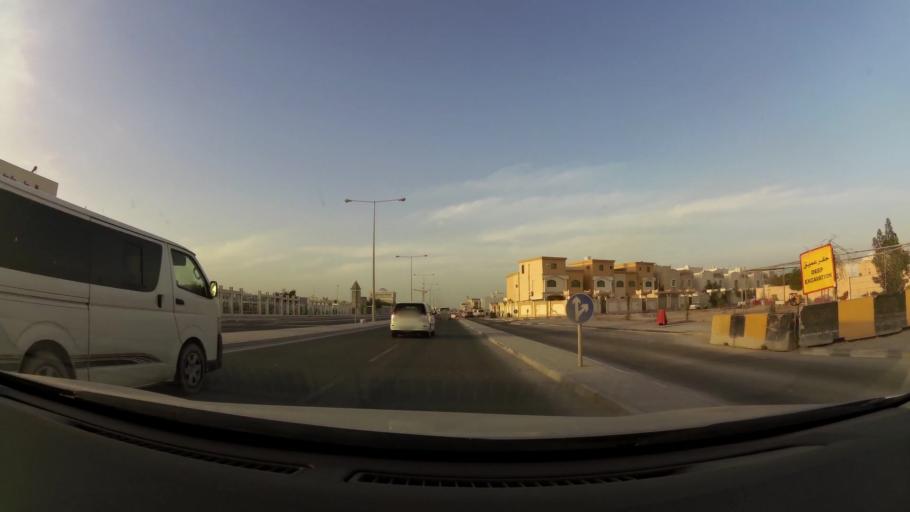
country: QA
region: Al Wakrah
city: Al Wakrah
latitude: 25.1653
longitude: 51.5903
